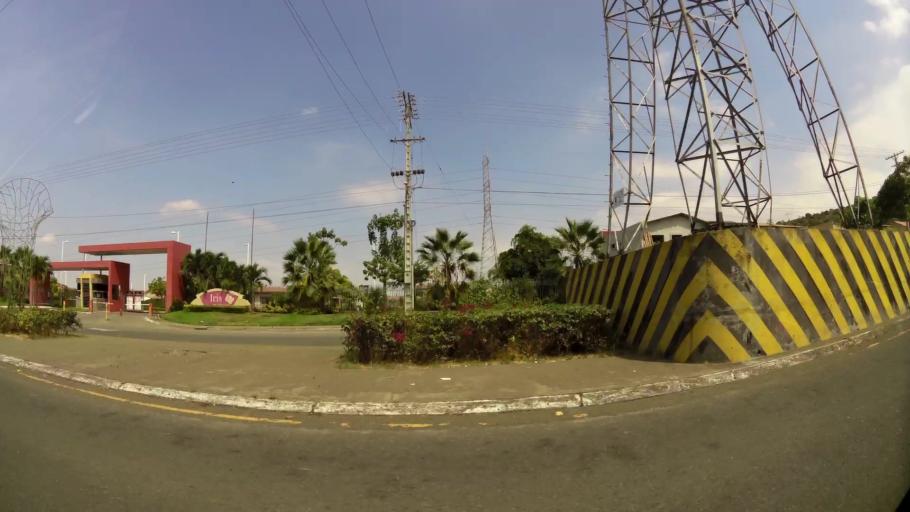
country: EC
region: Guayas
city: El Triunfo
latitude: -2.0342
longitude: -79.8984
